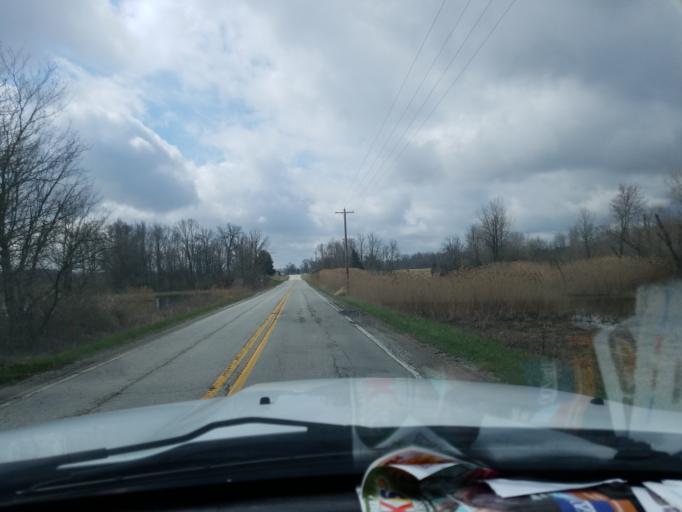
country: US
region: Indiana
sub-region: Sullivan County
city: Farmersburg
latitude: 39.3560
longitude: -87.3065
